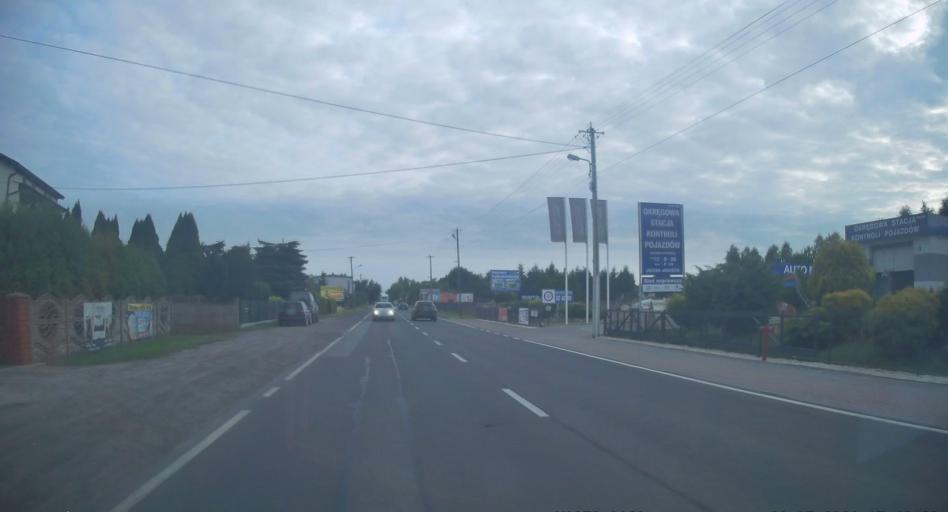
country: PL
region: Lodz Voivodeship
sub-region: Powiat radomszczanski
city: Radomsko
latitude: 51.1001
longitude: 19.4617
